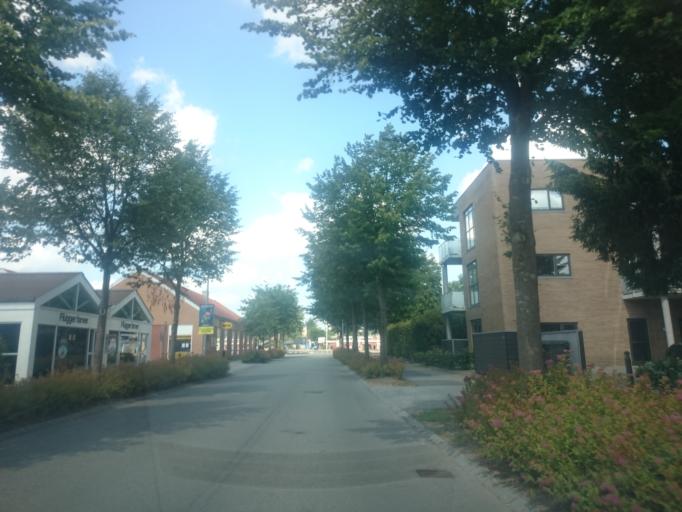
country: DK
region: South Denmark
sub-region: Billund Kommune
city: Billund
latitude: 55.7335
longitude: 9.1101
